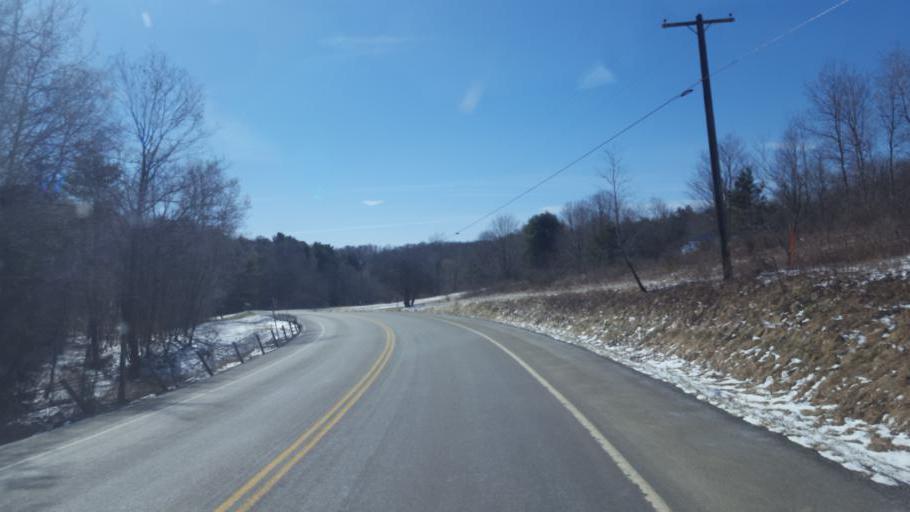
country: US
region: New York
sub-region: Allegany County
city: Andover
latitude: 42.0580
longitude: -77.7920
